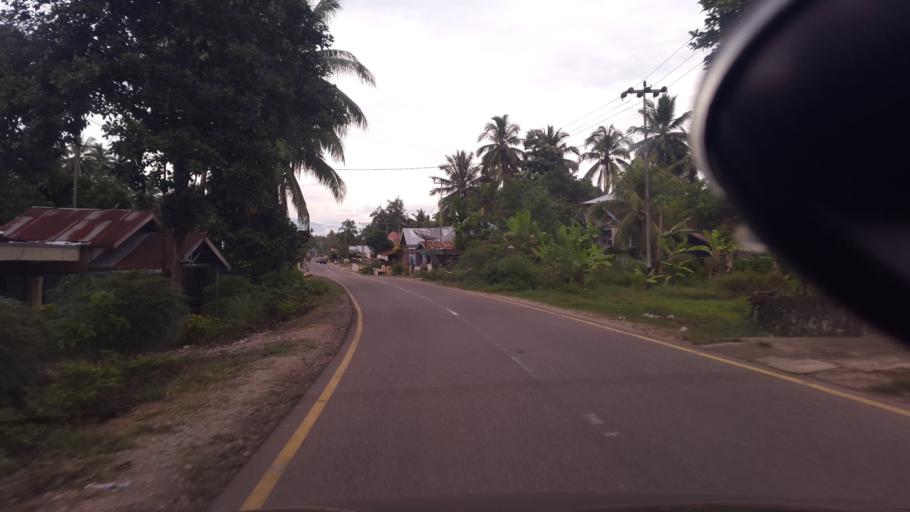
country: ID
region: West Sumatra
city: Singkarak
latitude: -0.7426
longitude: 100.6166
